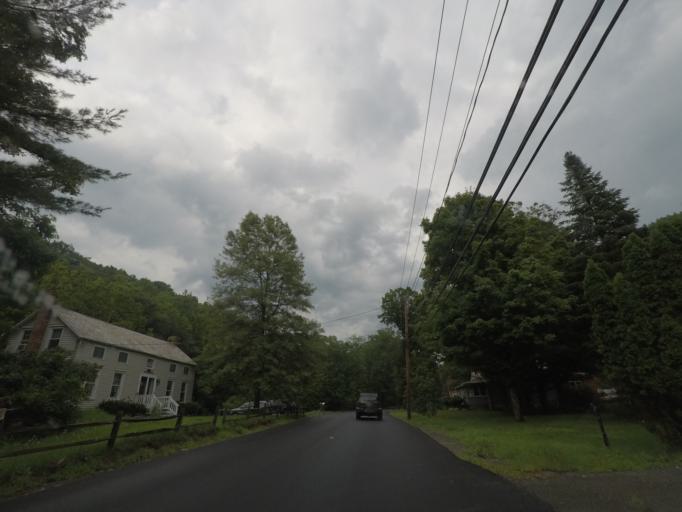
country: US
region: New York
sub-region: Rensselaer County
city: Poestenkill
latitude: 42.6887
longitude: -73.5544
